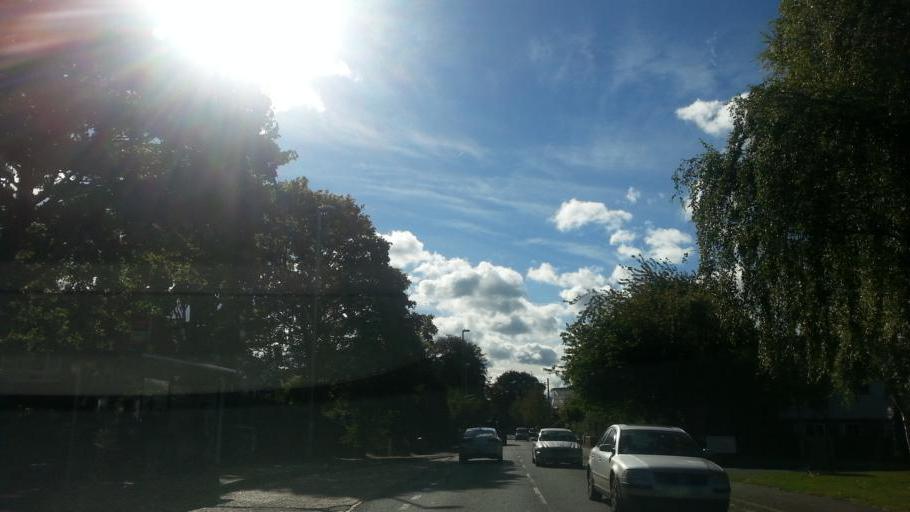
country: GB
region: England
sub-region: Cambridgeshire
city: Histon
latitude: 52.2279
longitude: 0.1119
